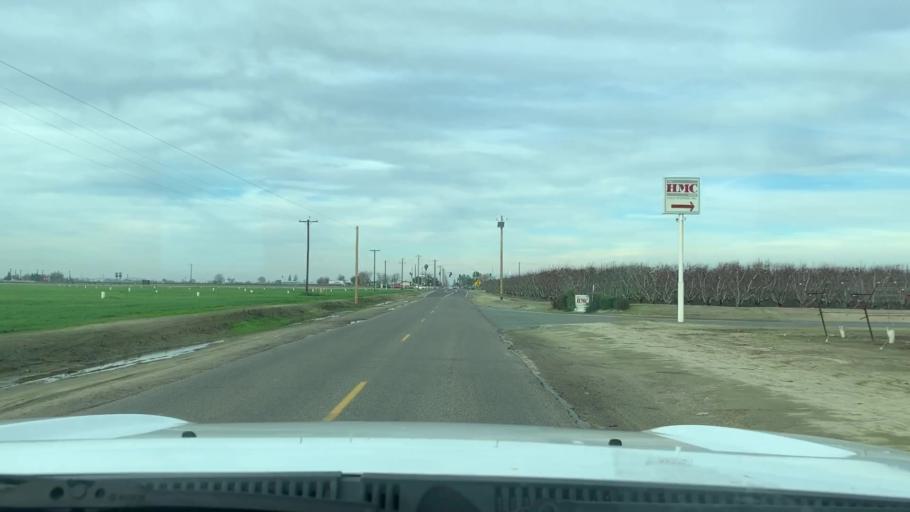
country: US
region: California
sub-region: Fresno County
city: Kingsburg
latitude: 36.5438
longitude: -119.5751
